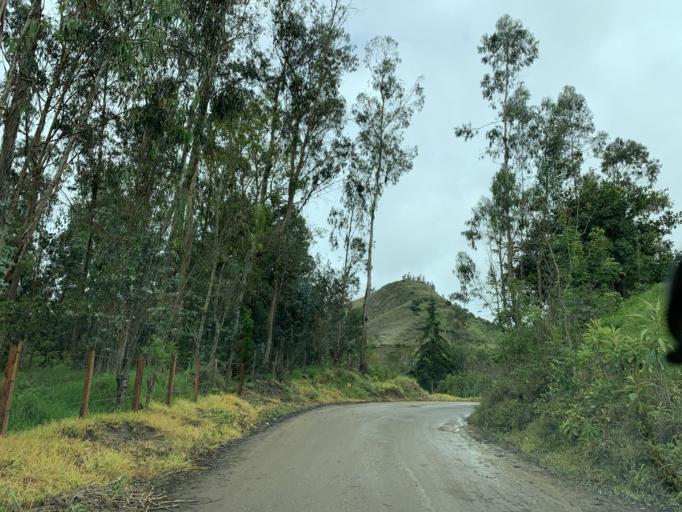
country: CO
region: Boyaca
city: Tibana
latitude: 5.3126
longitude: -73.4239
